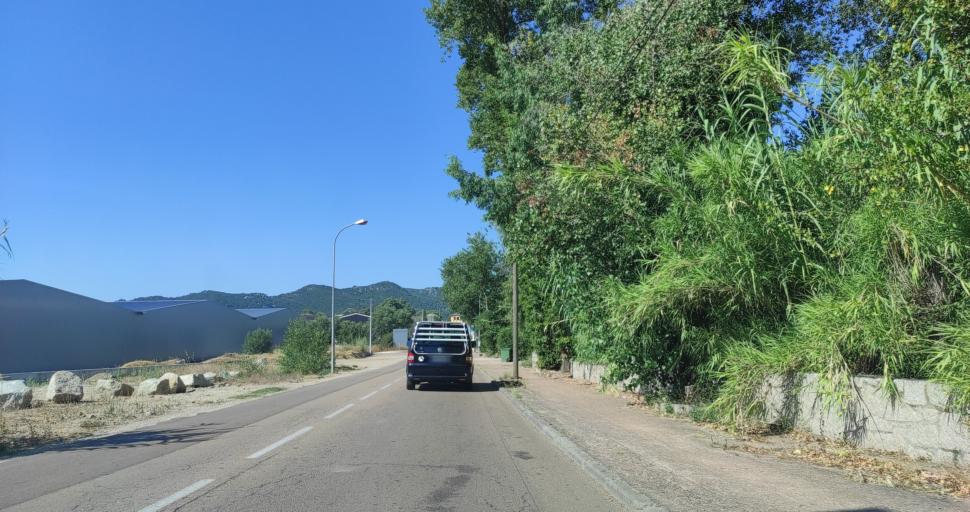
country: FR
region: Corsica
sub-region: Departement de la Corse-du-Sud
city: Porto-Vecchio
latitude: 41.5824
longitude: 9.2782
